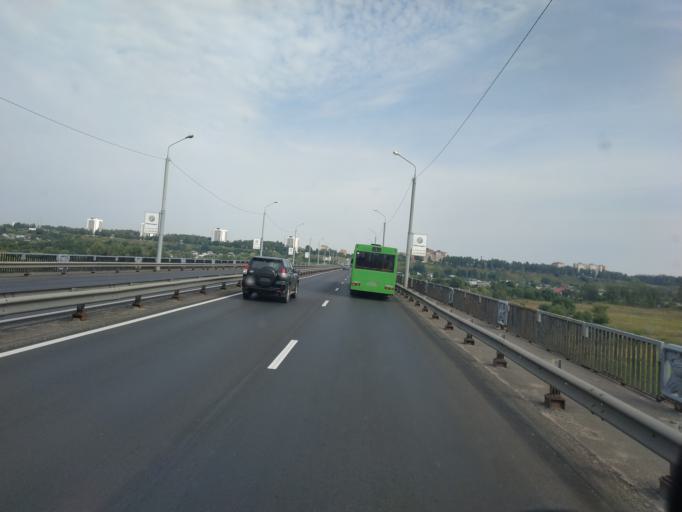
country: BY
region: Mogilev
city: Mahilyow
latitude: 53.8917
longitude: 30.3750
